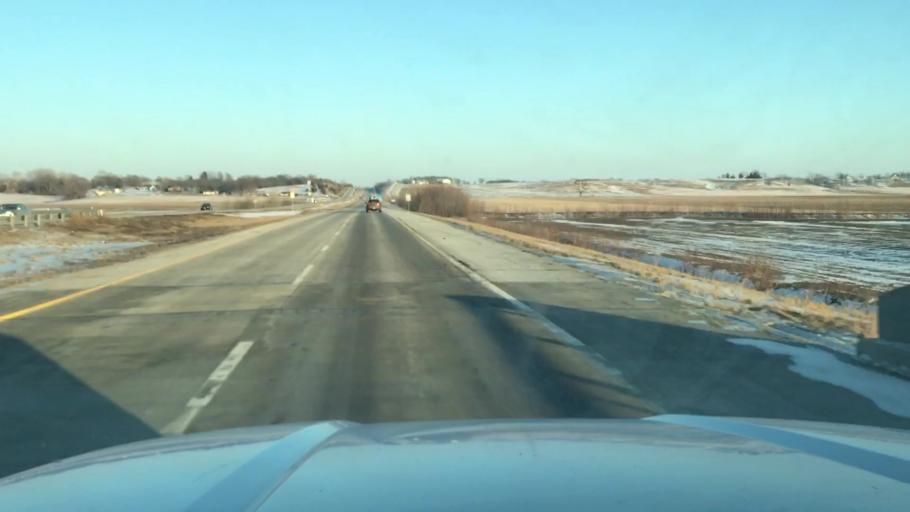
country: US
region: Missouri
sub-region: Buchanan County
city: Saint Joseph
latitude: 39.7478
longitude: -94.7243
